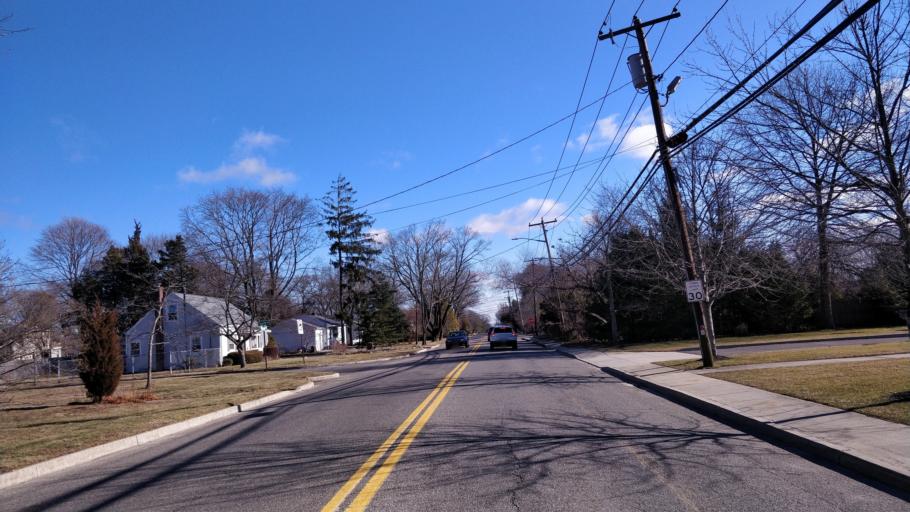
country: US
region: New York
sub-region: Suffolk County
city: Saint James
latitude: 40.8759
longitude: -73.1532
